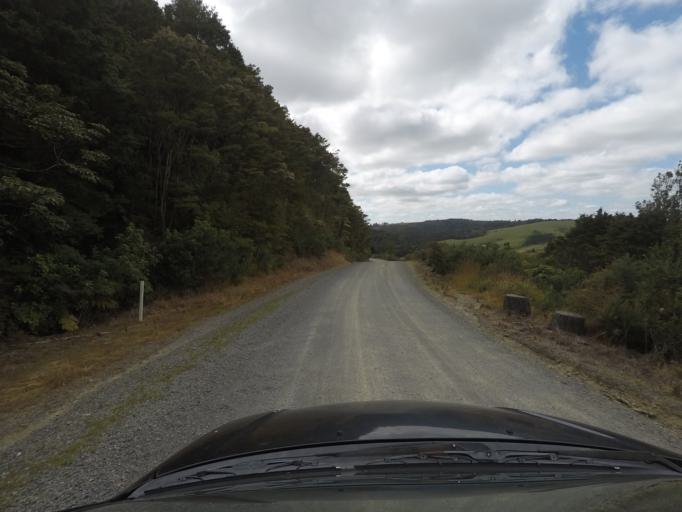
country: NZ
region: Northland
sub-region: Whangarei
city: Ruakaka
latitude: -35.9296
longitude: 174.3429
